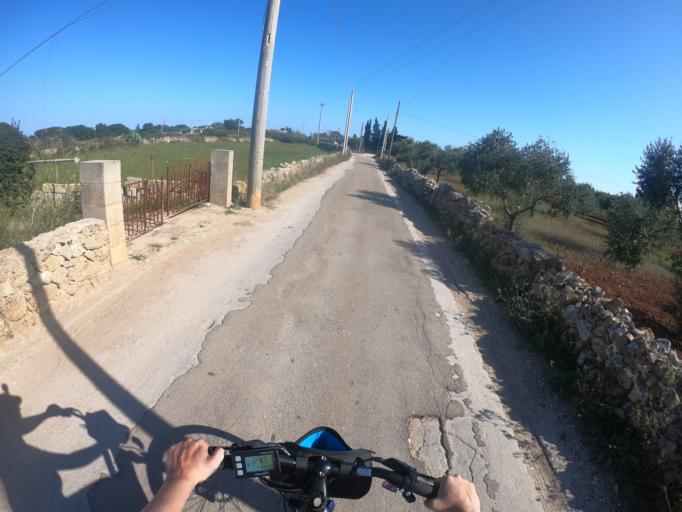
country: IT
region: Apulia
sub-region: Provincia di Lecce
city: Alessano
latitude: 39.8883
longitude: 18.3235
